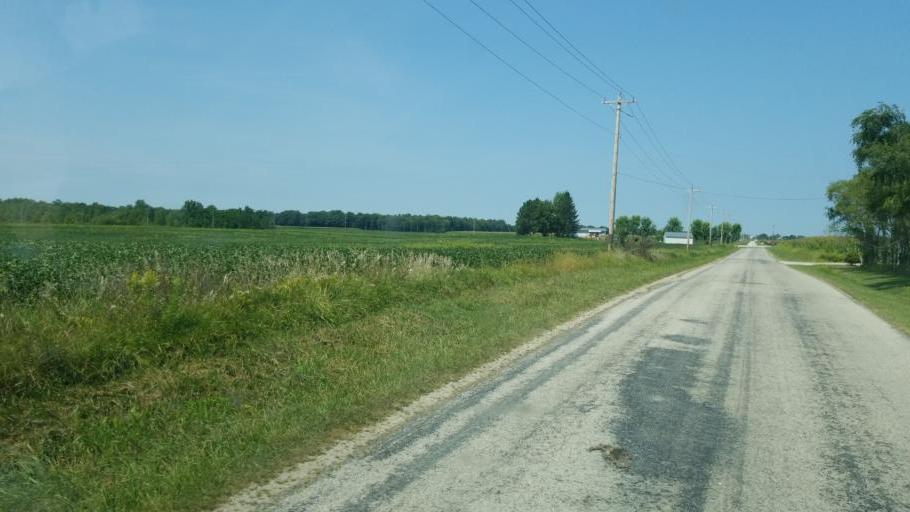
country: US
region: Ohio
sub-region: Crawford County
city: Bucyrus
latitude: 40.8403
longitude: -83.1123
